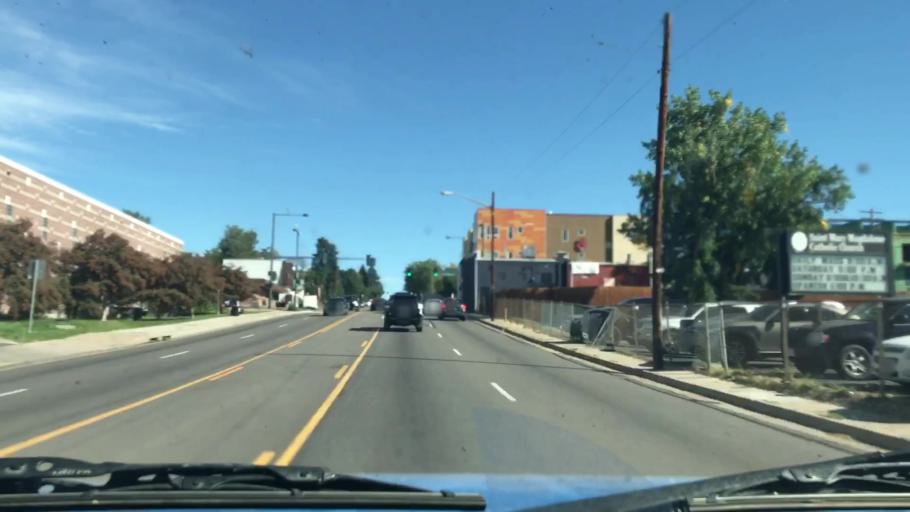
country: US
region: Colorado
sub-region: Jefferson County
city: Edgewater
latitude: 39.7574
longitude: -105.0532
